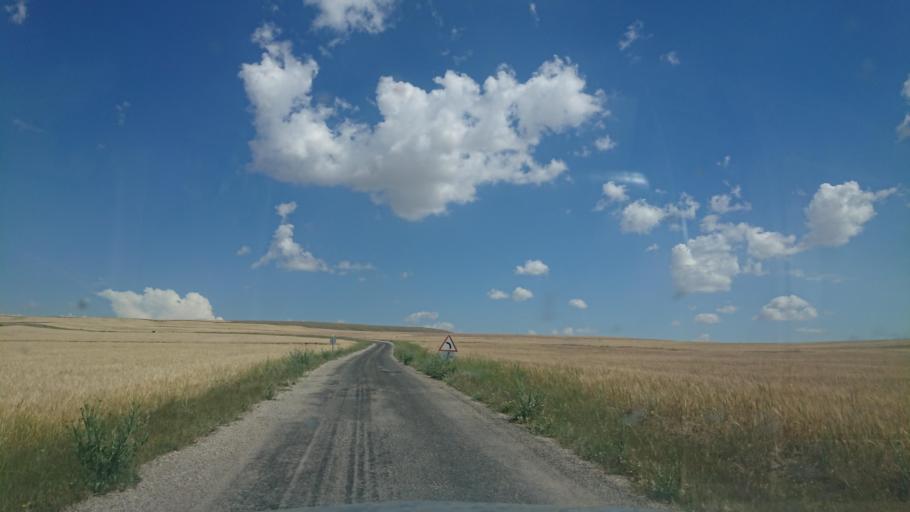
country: TR
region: Aksaray
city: Agacoren
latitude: 38.8074
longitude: 33.8005
